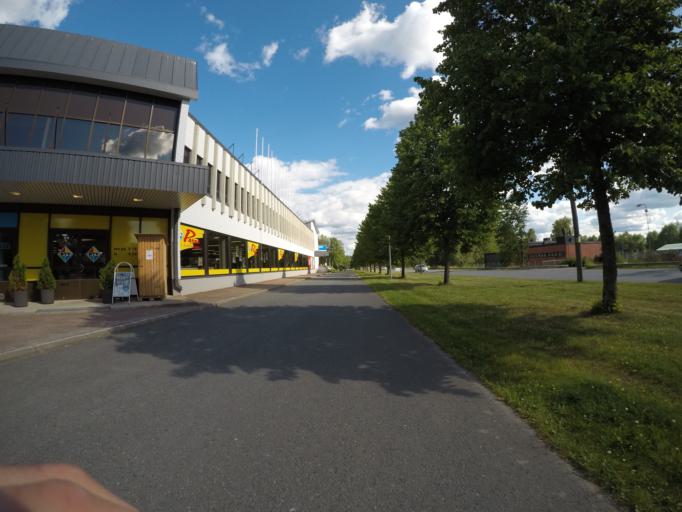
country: FI
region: Haeme
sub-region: Haemeenlinna
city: Haemeenlinna
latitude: 61.0004
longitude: 24.4879
